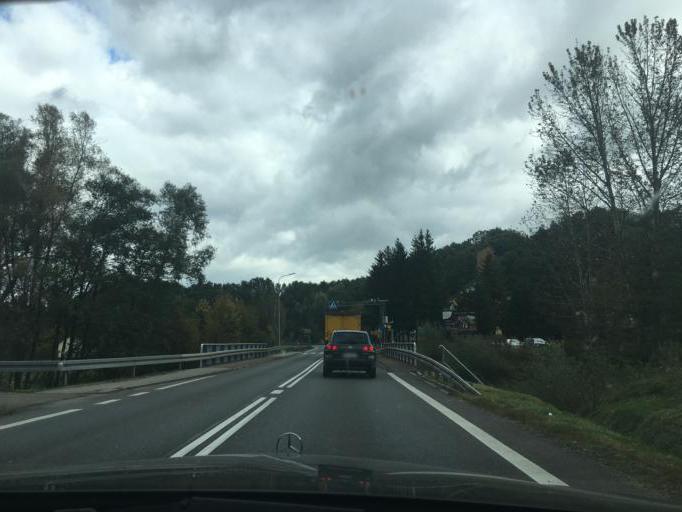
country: PL
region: Subcarpathian Voivodeship
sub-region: Powiat strzyzowski
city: Babica
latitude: 49.9198
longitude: 21.8787
